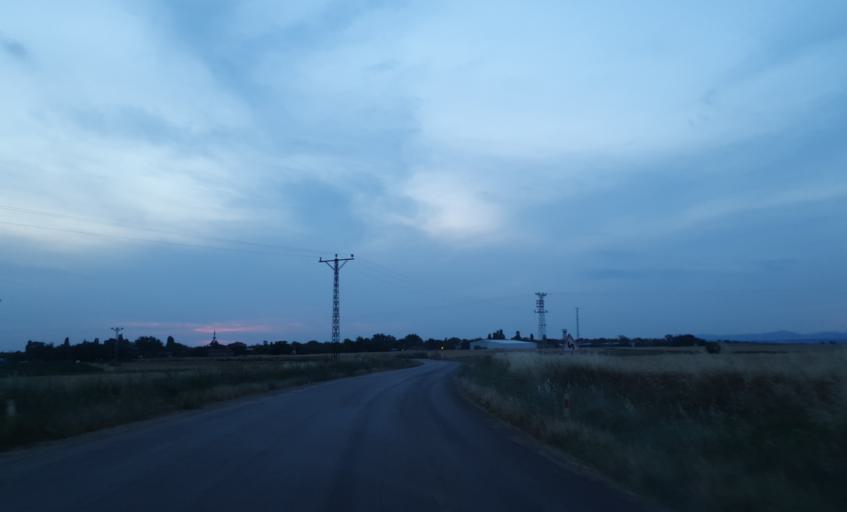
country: TR
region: Kirklareli
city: Vize
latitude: 41.5120
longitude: 27.7467
